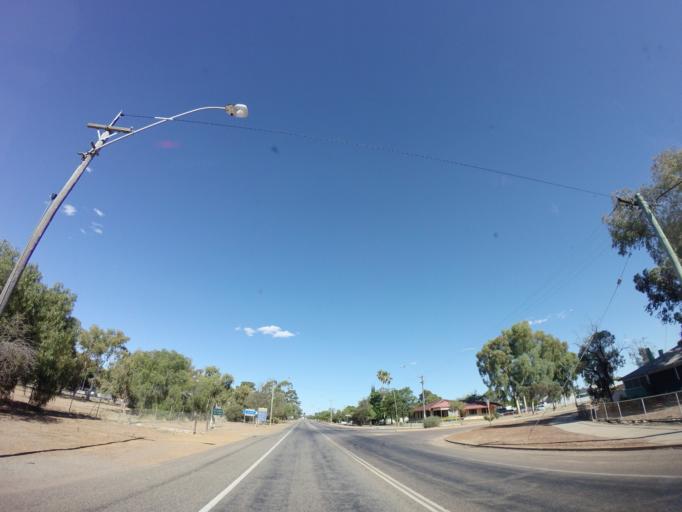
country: AU
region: Western Australia
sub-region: Merredin
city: Merredin
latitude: -31.4831
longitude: 118.2751
